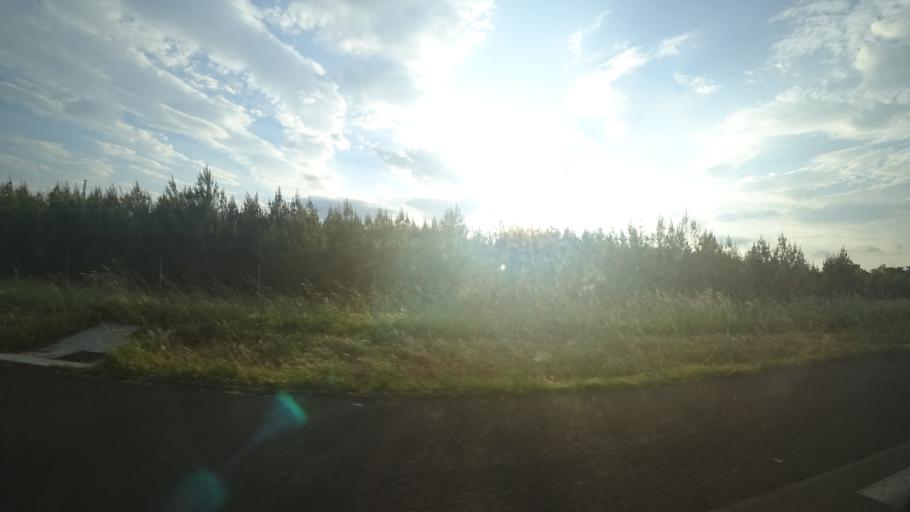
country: FR
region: Languedoc-Roussillon
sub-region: Departement de l'Herault
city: Aspiran
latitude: 43.5837
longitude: 3.4656
